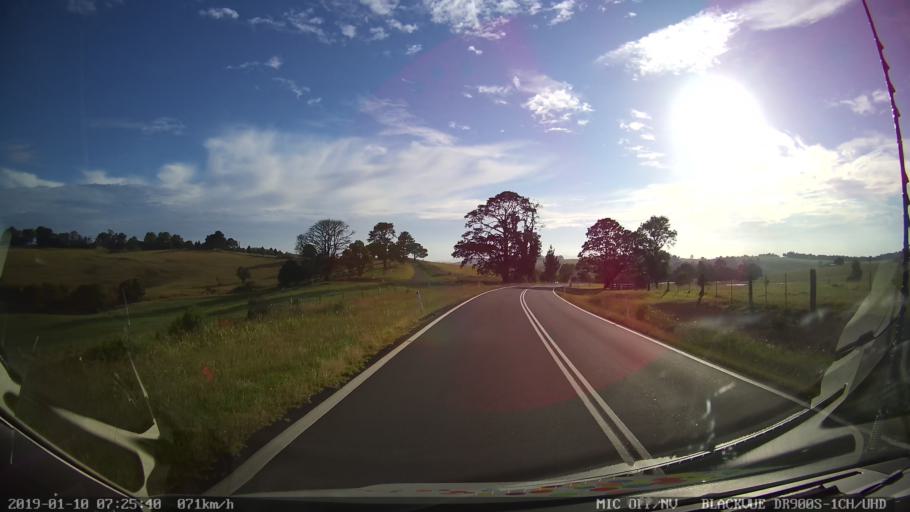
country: AU
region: New South Wales
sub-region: Bellingen
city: Dorrigo
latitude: -30.3687
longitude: 152.5917
